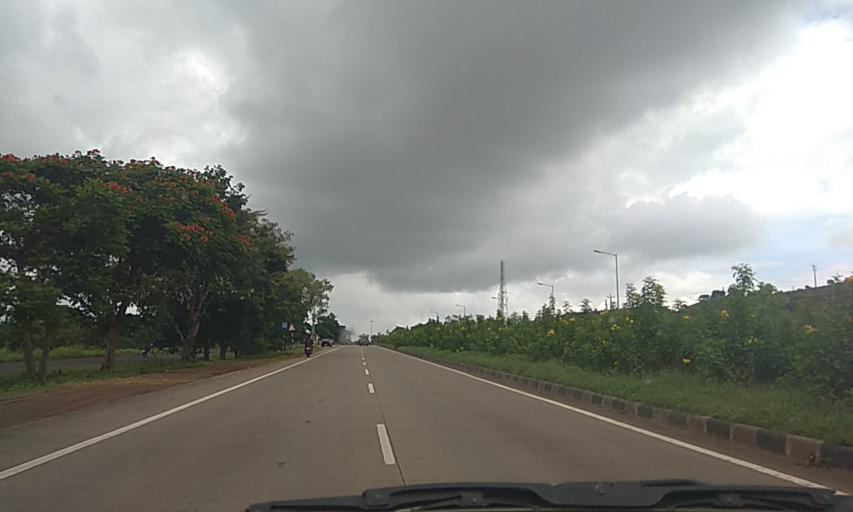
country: IN
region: Karnataka
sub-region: Belgaum
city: Sankeshwar
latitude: 16.2723
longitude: 74.4596
